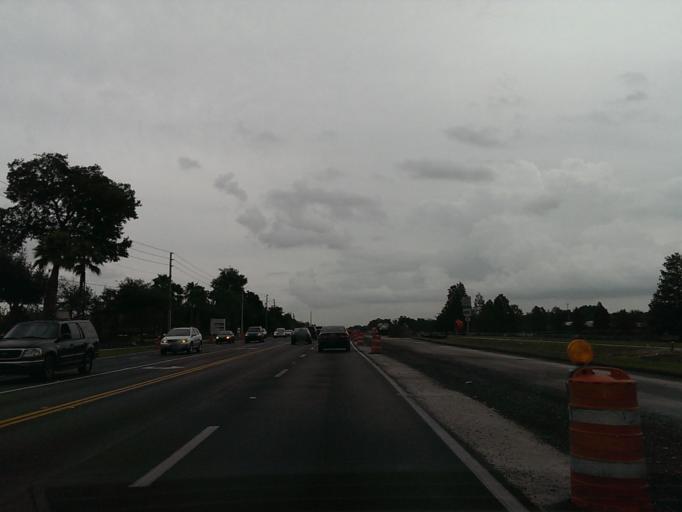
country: US
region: Florida
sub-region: Orange County
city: Ocoee
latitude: 28.5518
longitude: -81.5289
